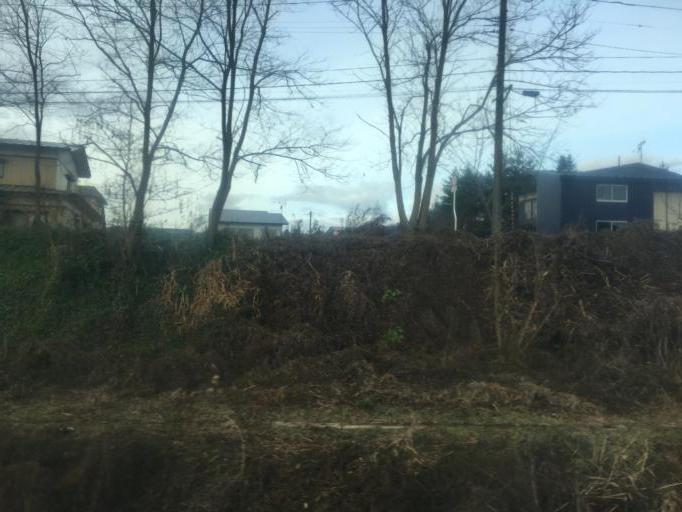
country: JP
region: Akita
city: Odate
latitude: 40.3007
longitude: 140.5676
